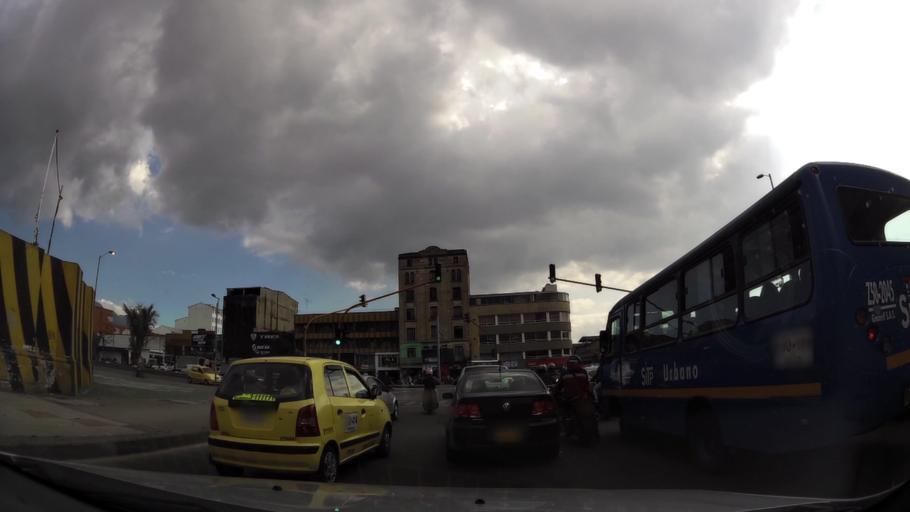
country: CO
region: Bogota D.C.
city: Bogota
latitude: 4.6070
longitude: -74.0830
